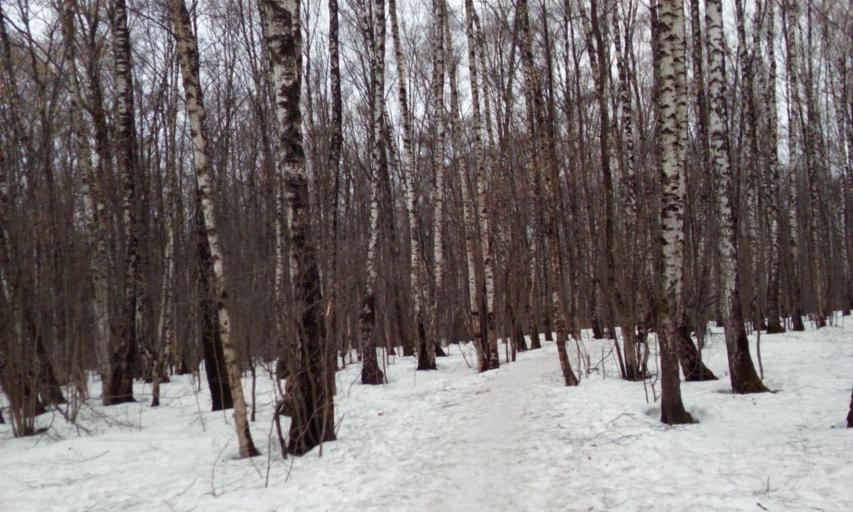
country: RU
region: Moscow
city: Tyoply Stan
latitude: 55.6378
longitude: 37.4878
